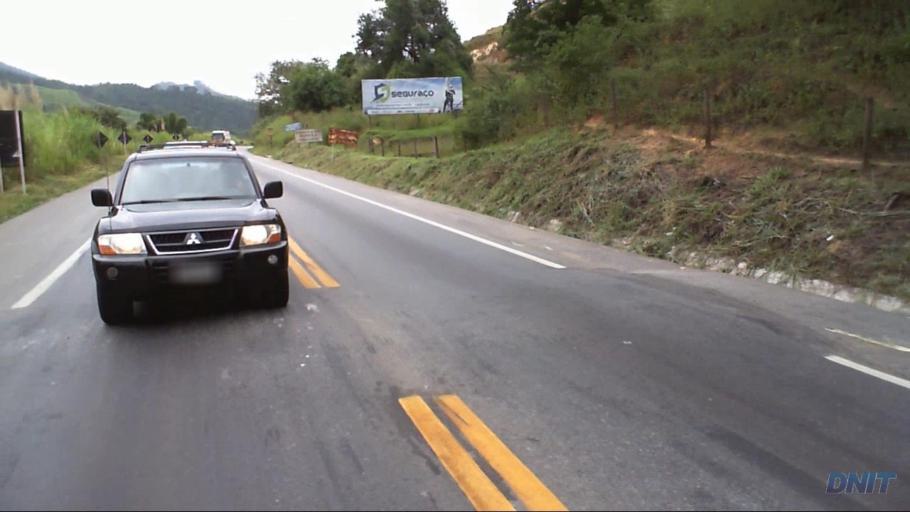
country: BR
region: Minas Gerais
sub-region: Timoteo
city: Timoteo
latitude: -19.6057
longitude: -42.7592
